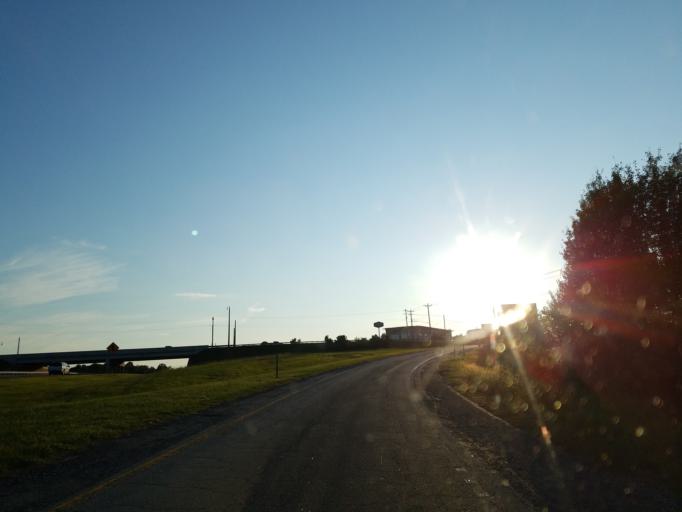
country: US
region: South Carolina
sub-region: Cherokee County
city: Gaffney
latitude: 35.0838
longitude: -81.7043
